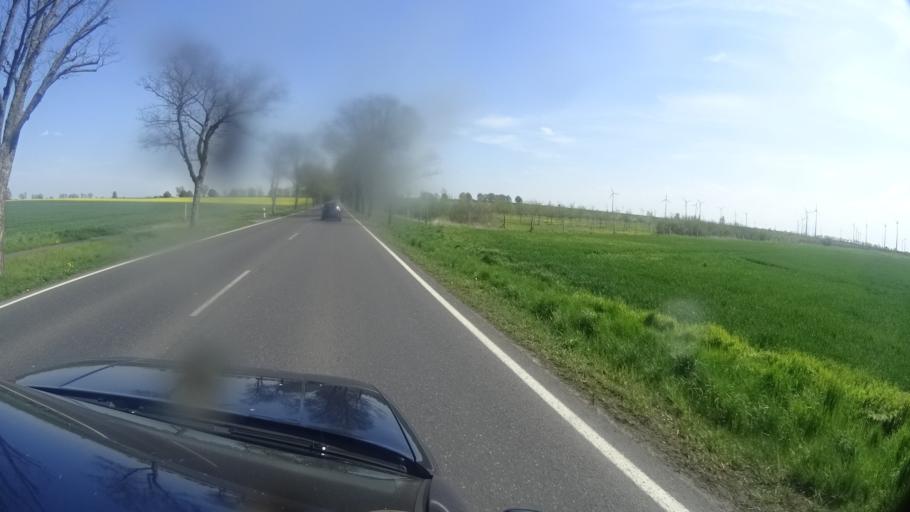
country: DE
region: Brandenburg
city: Nauen
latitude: 52.6193
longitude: 12.8060
